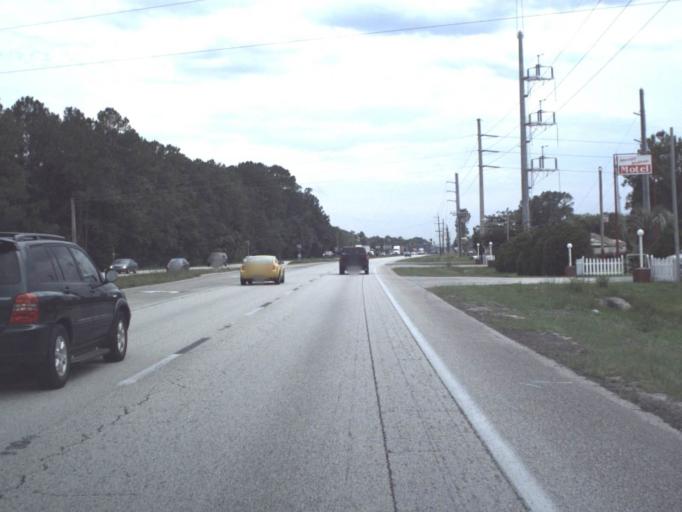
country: US
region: Florida
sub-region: Bradford County
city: Starke
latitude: 29.9726
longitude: -82.1014
